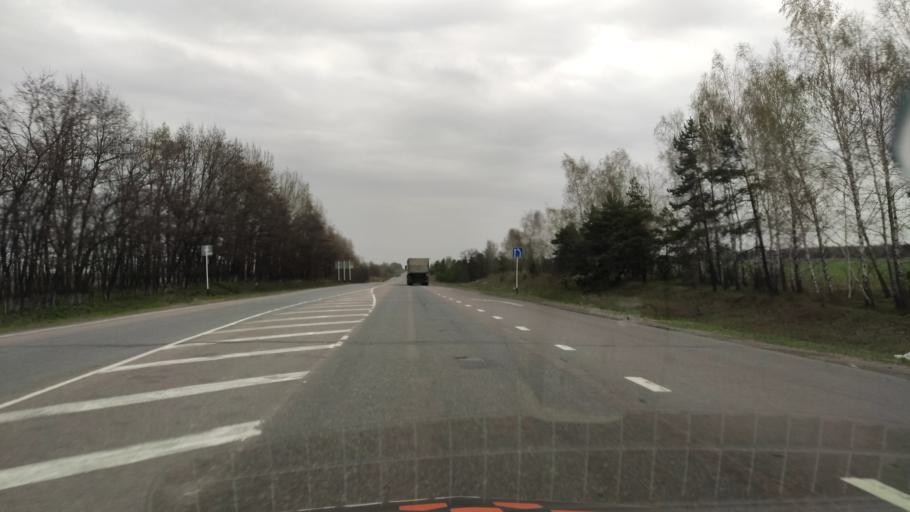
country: RU
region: Belgorod
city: Staryy Oskol
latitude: 51.4376
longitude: 37.9052
